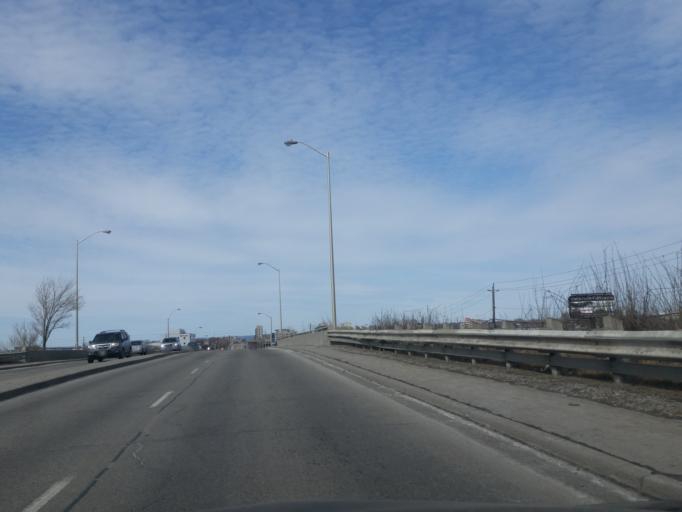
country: CA
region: Ontario
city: Ottawa
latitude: 45.4084
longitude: -75.6283
